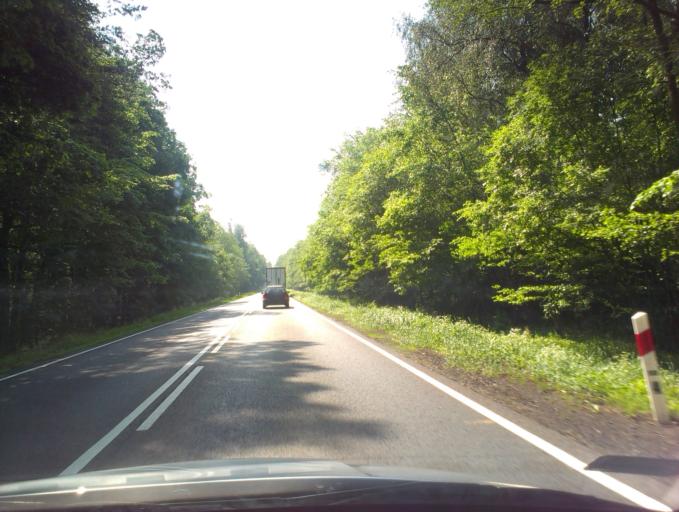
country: PL
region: West Pomeranian Voivodeship
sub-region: Powiat szczecinecki
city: Szczecinek
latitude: 53.6297
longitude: 16.7719
